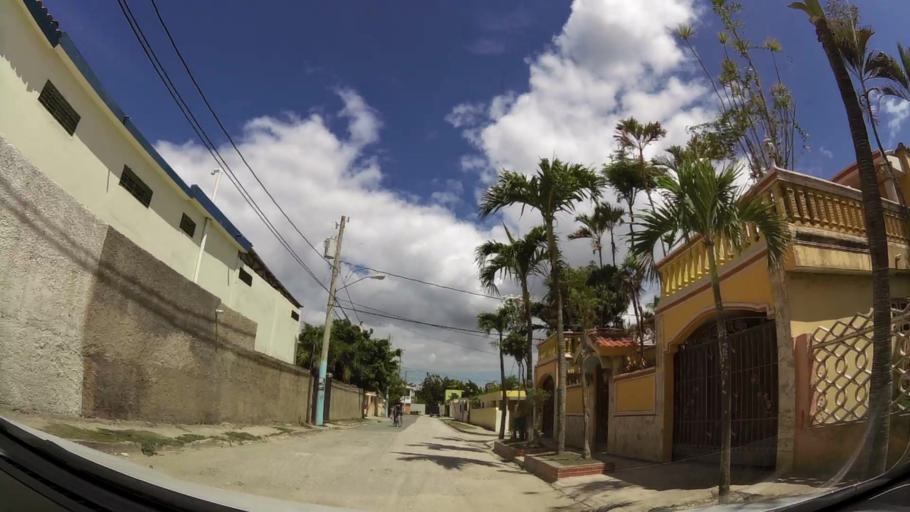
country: DO
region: Santo Domingo
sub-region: Santo Domingo
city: Boca Chica
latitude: 18.4492
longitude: -69.6535
